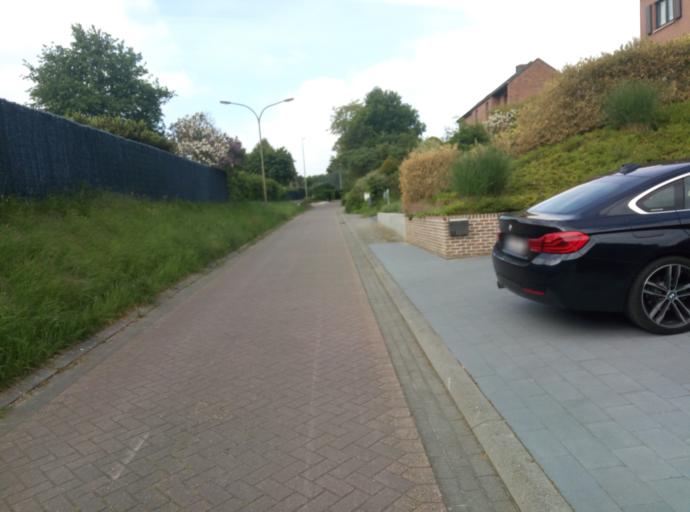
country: BE
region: Flanders
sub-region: Provincie Vlaams-Brabant
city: Bierbeek
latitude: 50.8522
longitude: 4.7566
